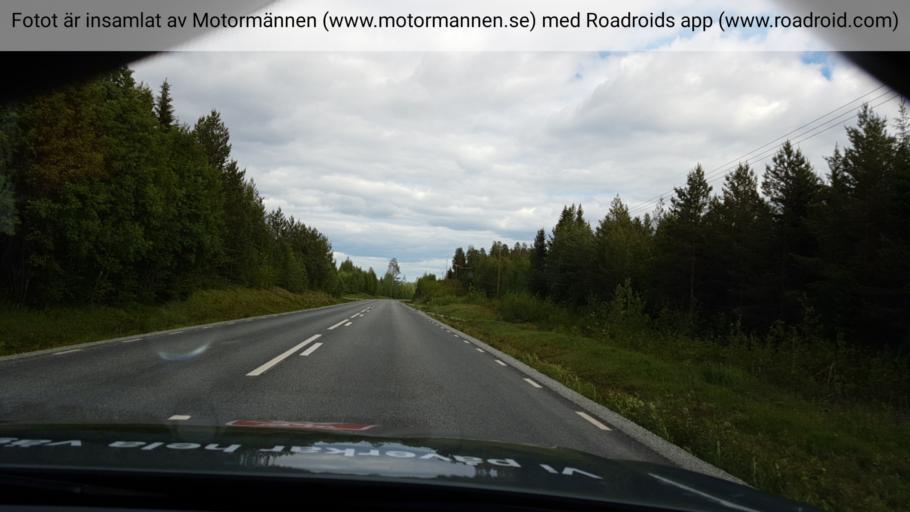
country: SE
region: Jaemtland
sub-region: Stroemsunds Kommun
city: Stroemsund
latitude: 64.1974
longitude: 15.6128
